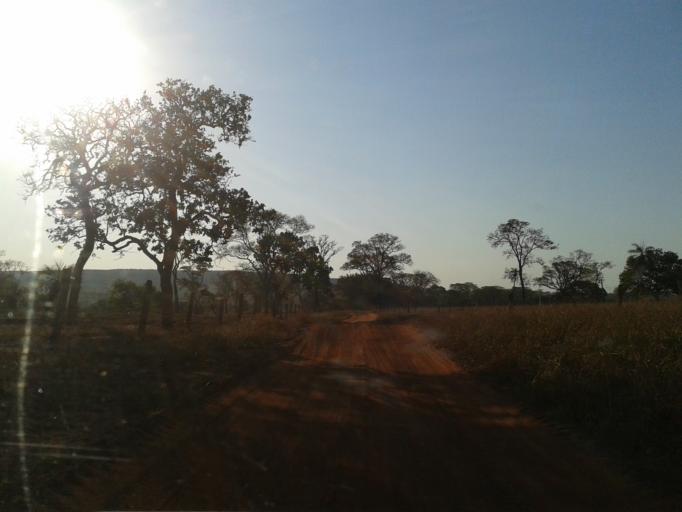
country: BR
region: Minas Gerais
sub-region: Ituiutaba
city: Ituiutaba
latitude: -19.2441
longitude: -49.5999
